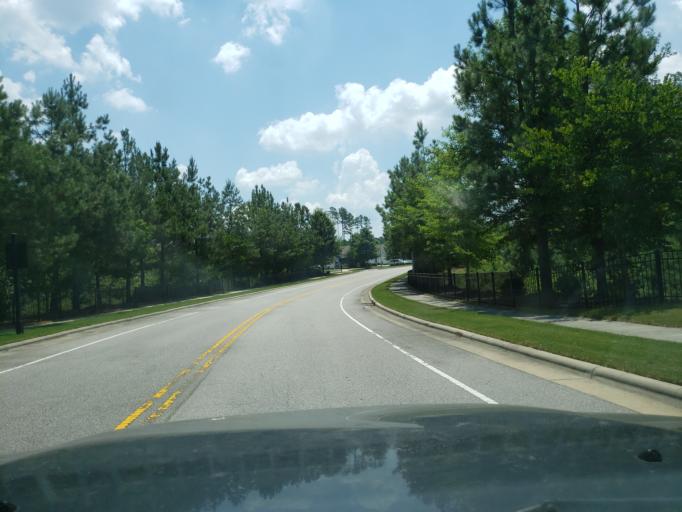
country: US
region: North Carolina
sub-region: Wake County
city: Green Level
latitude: 35.8382
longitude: -78.9129
